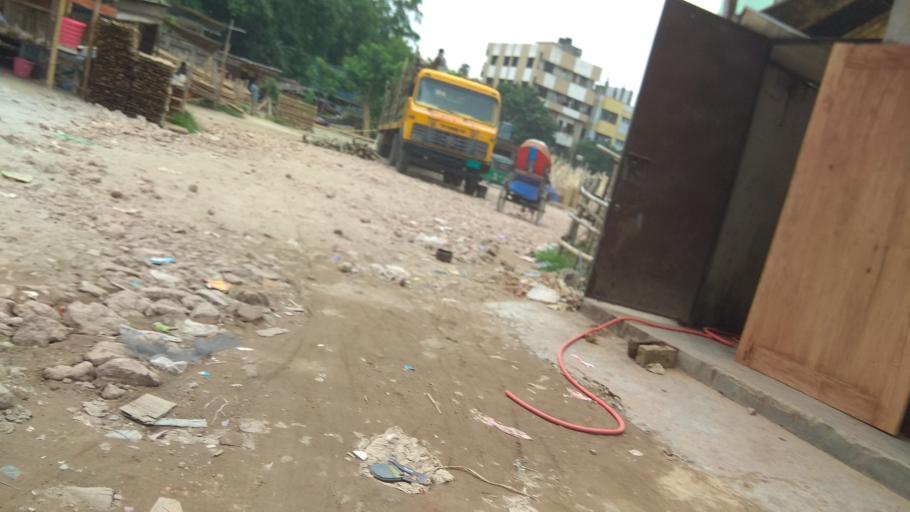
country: BD
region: Dhaka
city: Tungi
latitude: 23.8236
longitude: 90.3527
